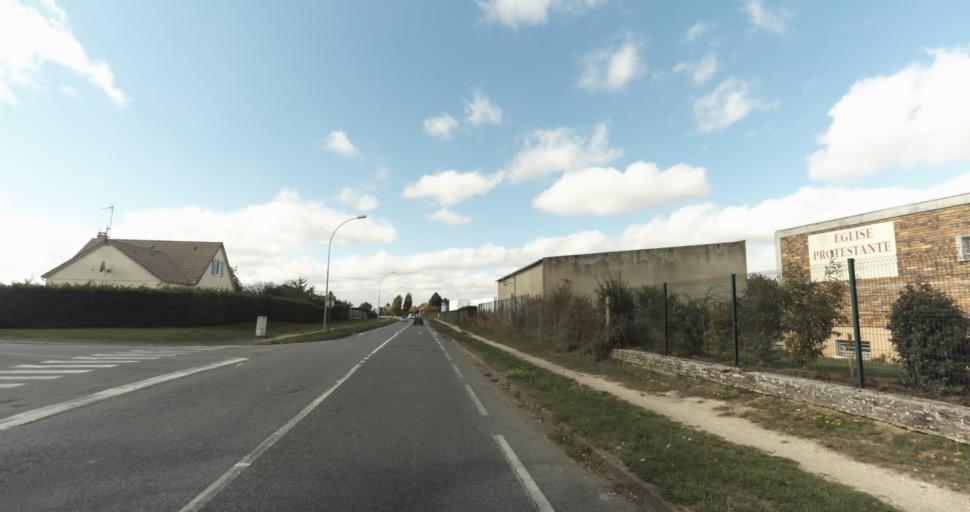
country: FR
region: Centre
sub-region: Departement d'Eure-et-Loir
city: Garnay
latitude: 48.7292
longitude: 1.3264
